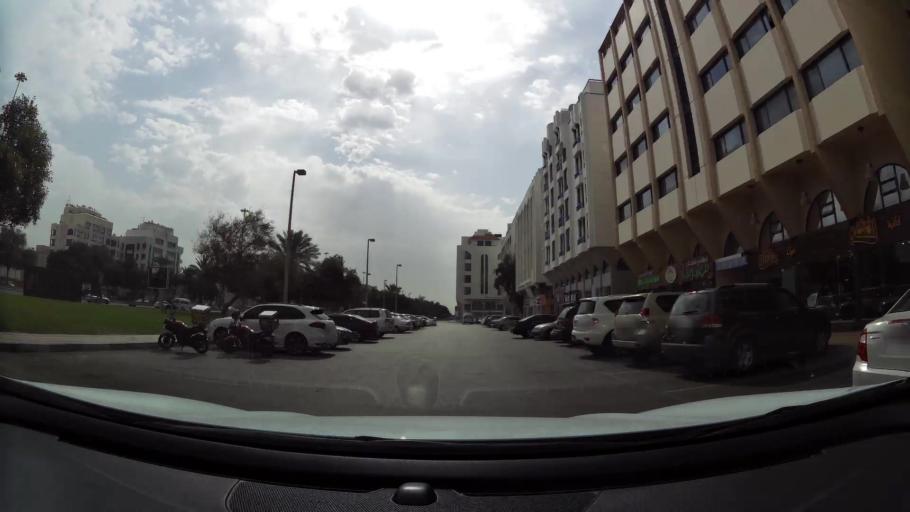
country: AE
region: Abu Dhabi
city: Abu Dhabi
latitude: 24.4559
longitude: 54.3833
